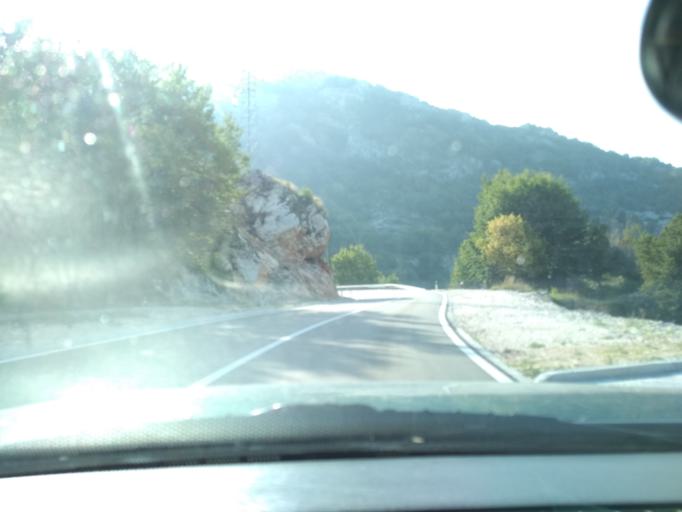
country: ME
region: Cetinje
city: Cetinje
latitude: 42.4308
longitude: 18.8621
